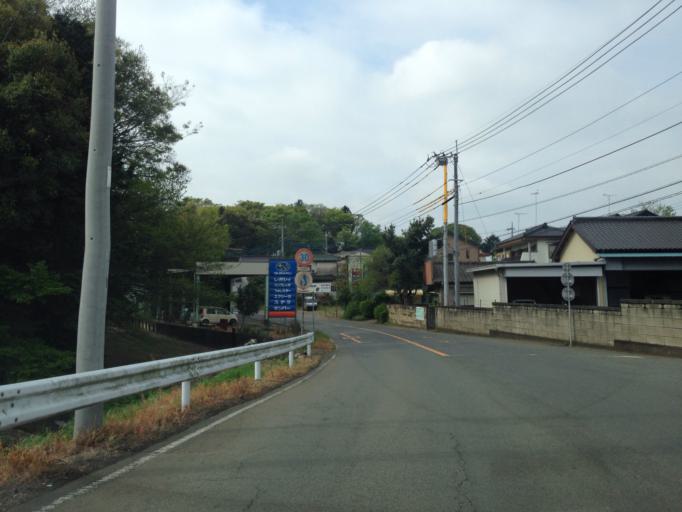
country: JP
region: Ibaraki
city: Sakai
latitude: 36.1653
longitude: 139.8368
